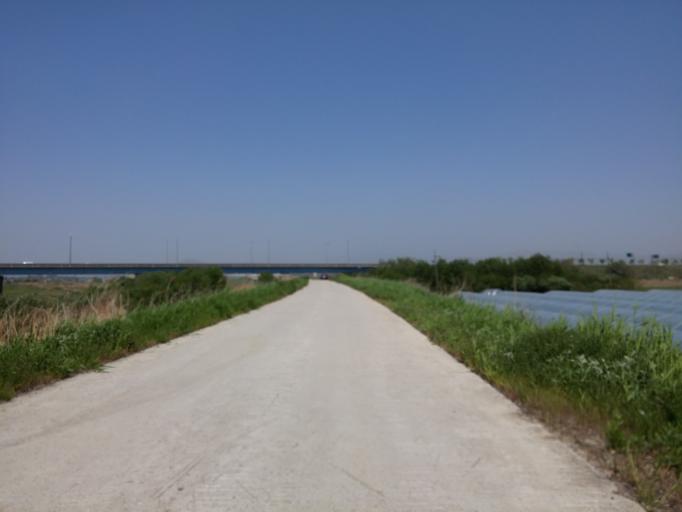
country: KR
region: Chungcheongnam-do
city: Nonsan
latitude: 36.2171
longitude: 127.0933
